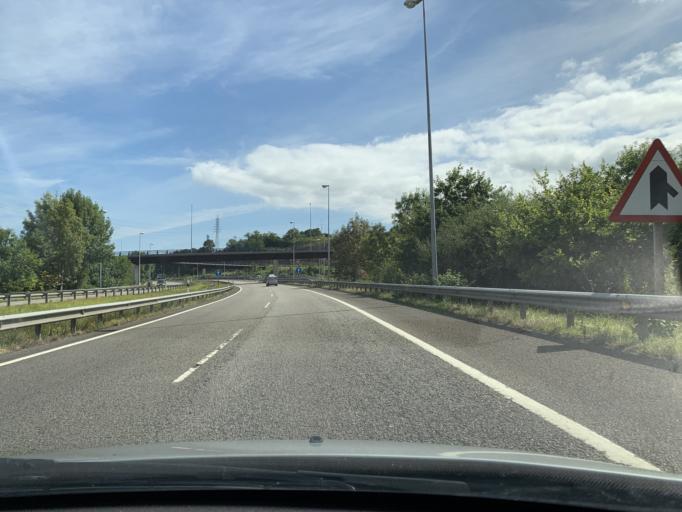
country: ES
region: Asturias
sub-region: Province of Asturias
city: Gijon
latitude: 43.5153
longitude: -5.6581
